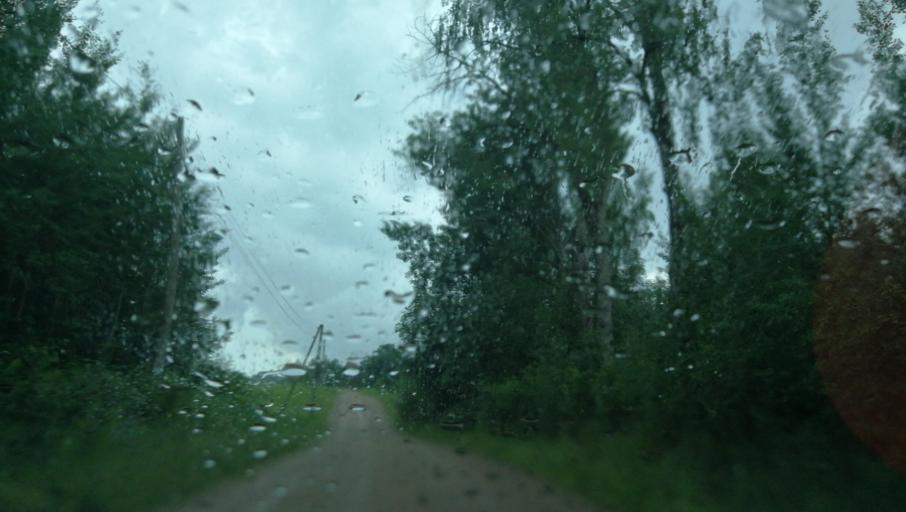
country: LV
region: Vecpiebalga
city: Vecpiebalga
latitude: 57.1020
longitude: 25.6920
